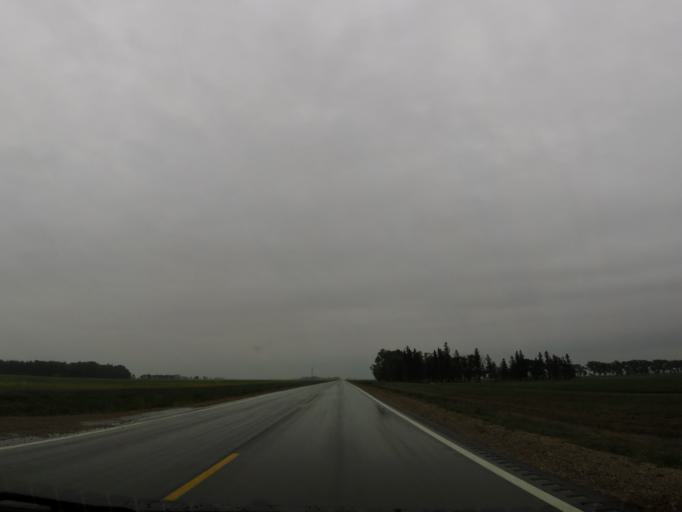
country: US
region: Minnesota
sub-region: Kittson County
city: Hallock
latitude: 48.4569
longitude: -97.0533
